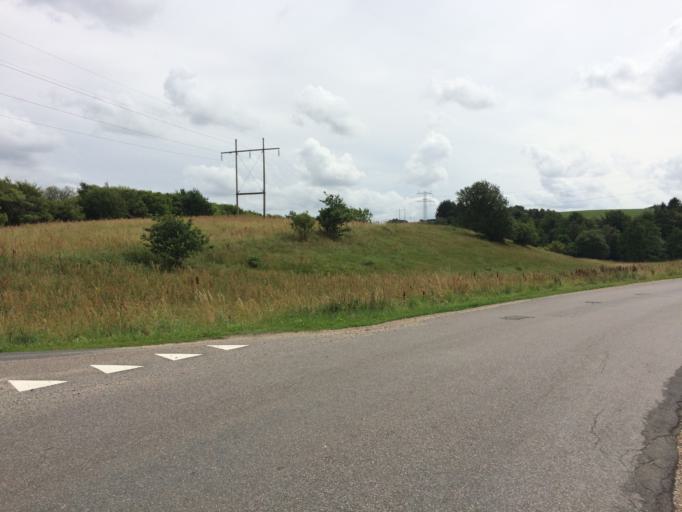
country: DK
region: Central Jutland
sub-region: Viborg Kommune
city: Viborg
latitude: 56.4921
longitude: 9.5234
